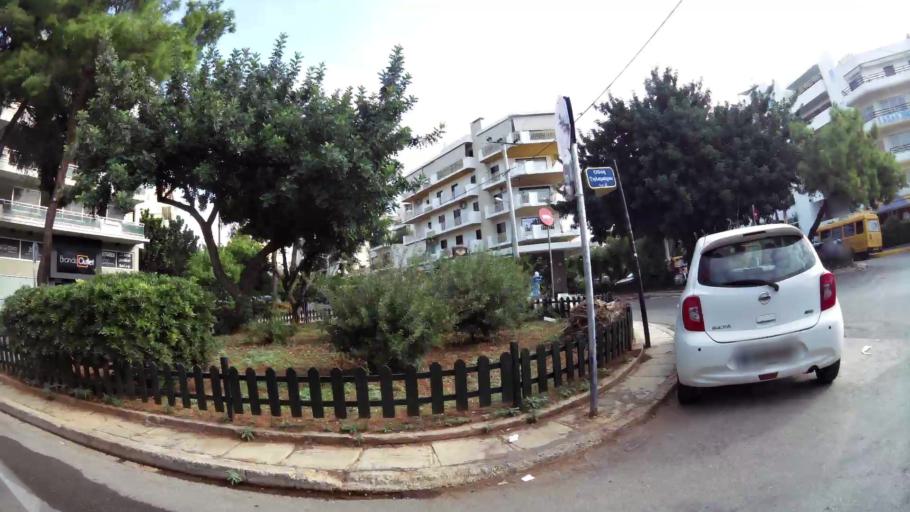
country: GR
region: Attica
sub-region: Nomarchia Athinas
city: Nea Smyrni
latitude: 37.9395
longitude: 23.7049
